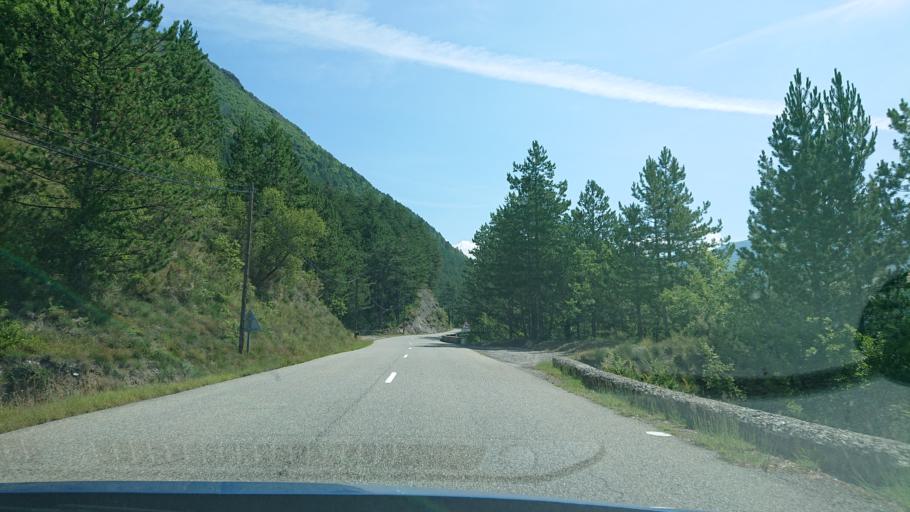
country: FR
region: Provence-Alpes-Cote d'Azur
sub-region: Departement des Alpes-de-Haute-Provence
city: Sisteron
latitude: 44.2667
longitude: 5.9872
